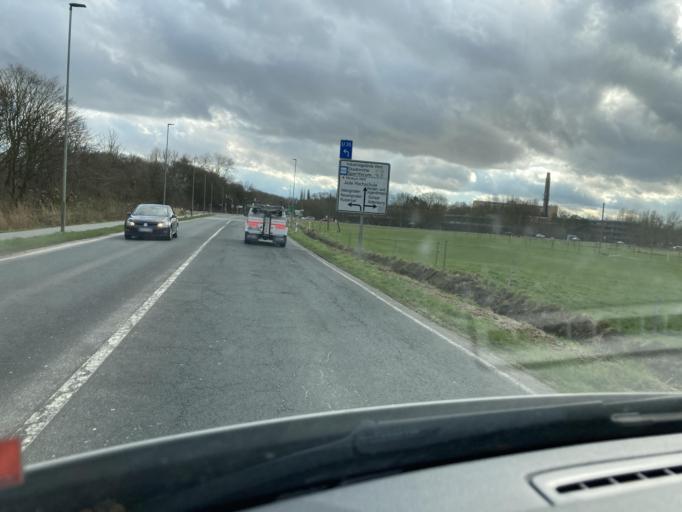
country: DE
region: Lower Saxony
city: Wilhelmshaven
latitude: 53.5515
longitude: 8.0838
